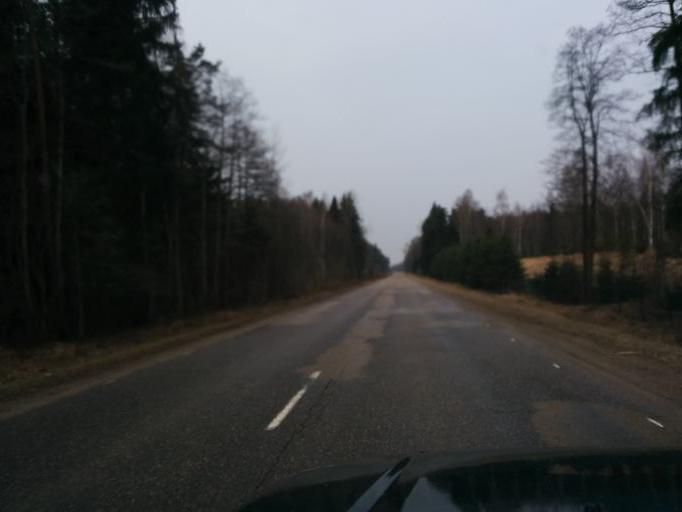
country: LV
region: Ikskile
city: Ikskile
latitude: 56.8085
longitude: 24.4893
